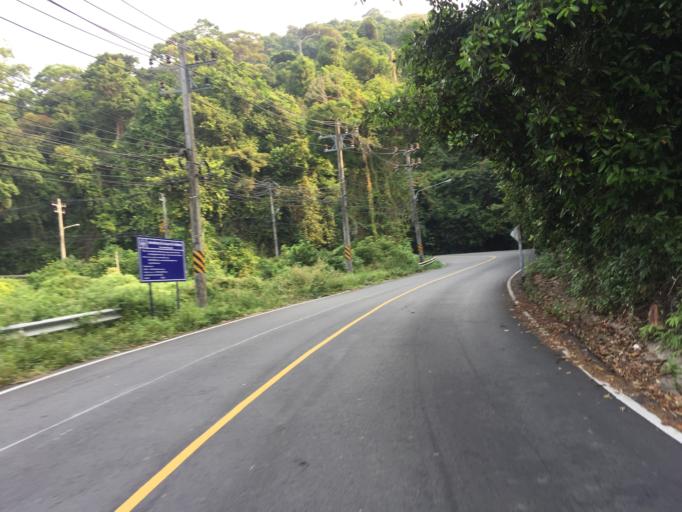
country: TH
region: Trat
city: Laem Ngop
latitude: 12.1162
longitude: 102.2683
